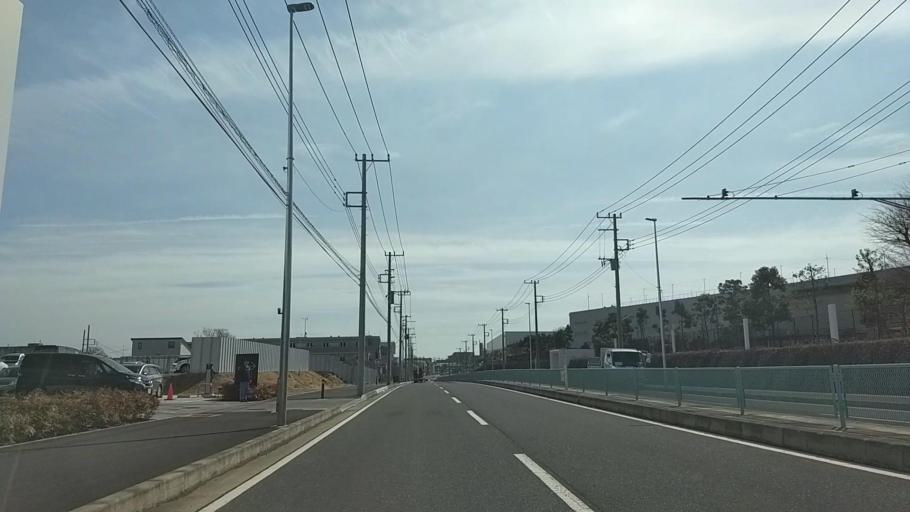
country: JP
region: Kanagawa
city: Fujisawa
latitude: 35.3989
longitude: 139.4564
